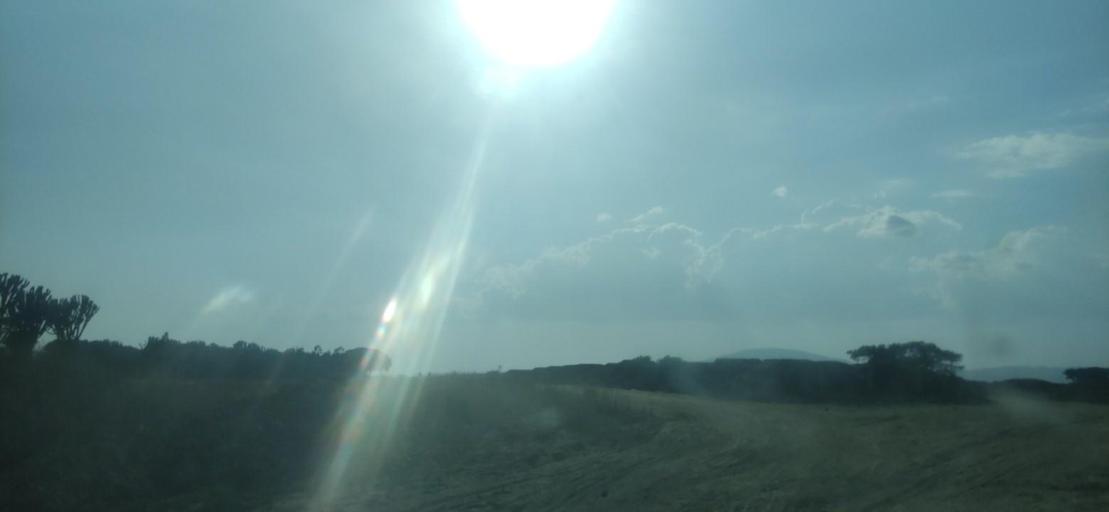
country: ET
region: Oromiya
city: Shashemene
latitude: 7.2042
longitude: 38.5417
